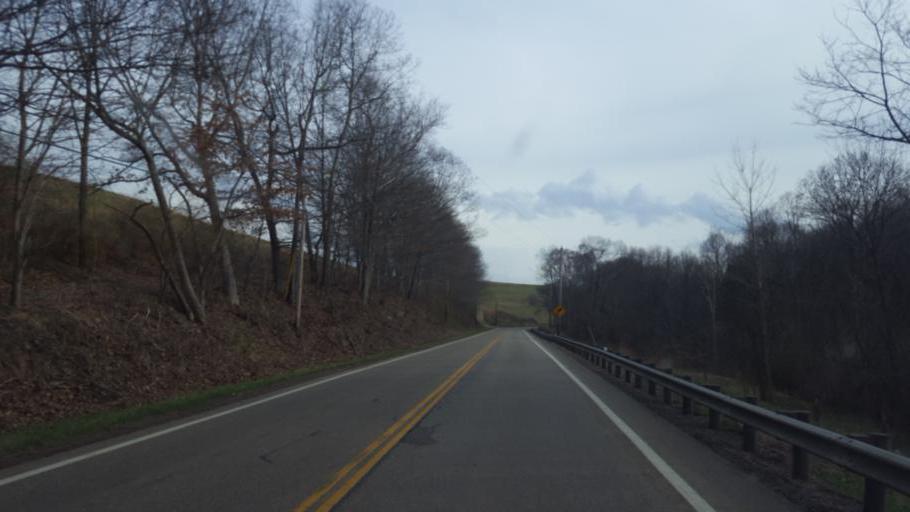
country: US
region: Ohio
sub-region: Coshocton County
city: Coshocton
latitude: 40.2161
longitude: -81.8347
